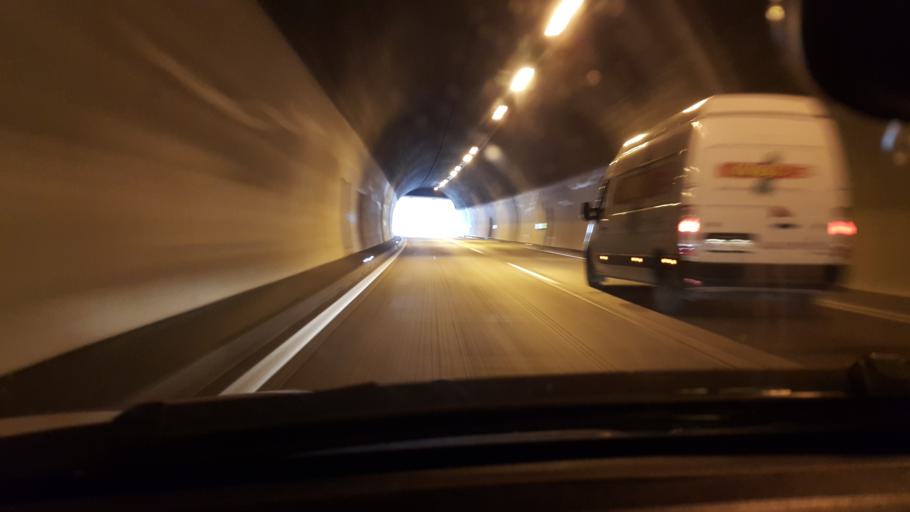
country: SI
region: Vransko
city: Vransko
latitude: 46.2100
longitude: 14.9076
